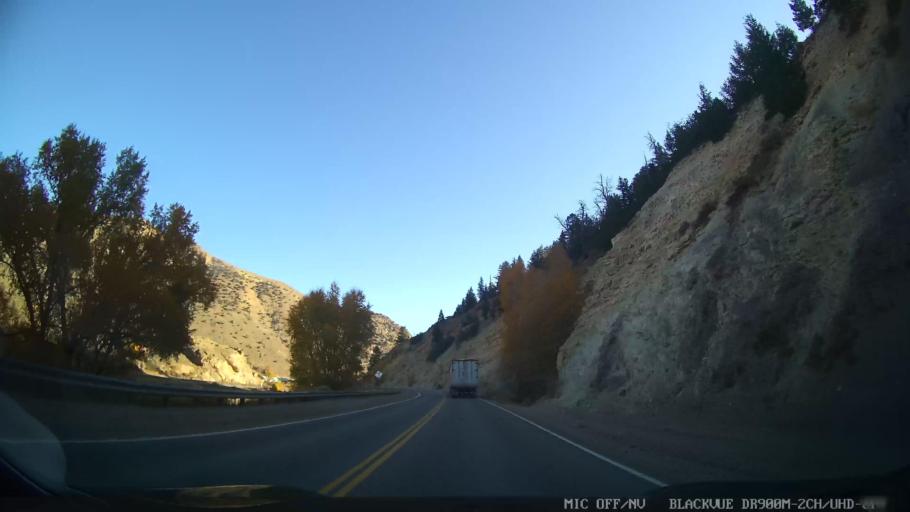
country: US
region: Colorado
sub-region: Grand County
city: Hot Sulphur Springs
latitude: 40.0705
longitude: -106.1119
